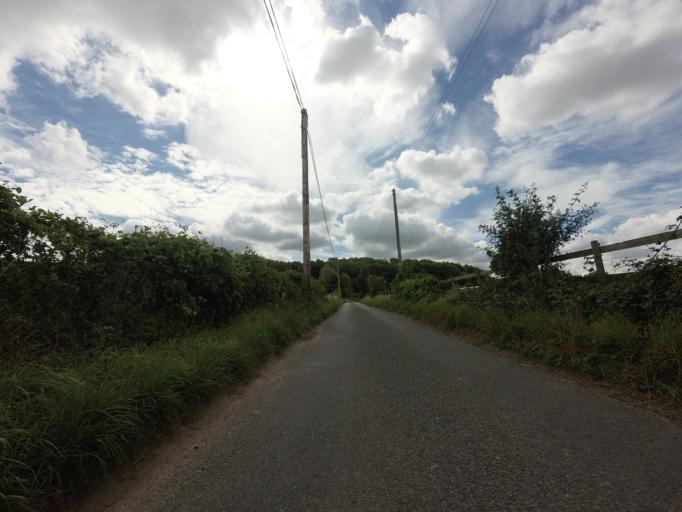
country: GB
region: England
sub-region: Kent
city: Swanley
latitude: 51.3698
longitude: 0.1433
